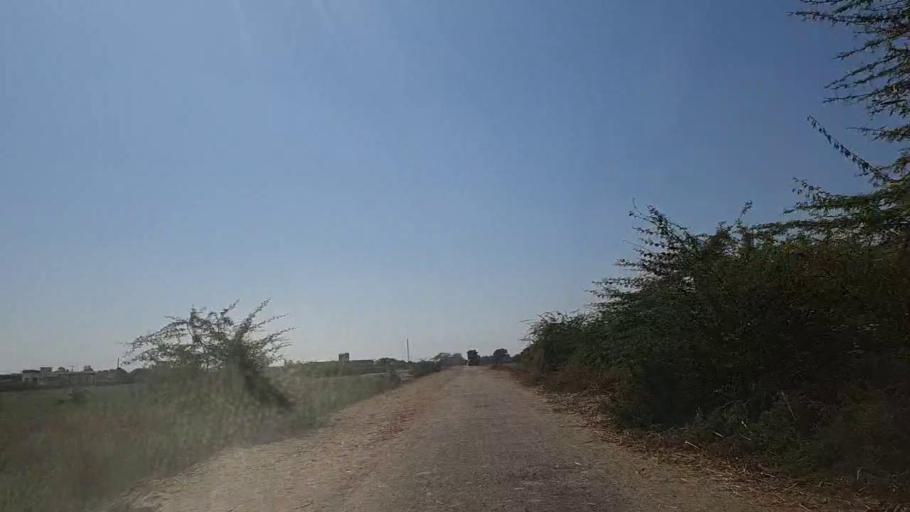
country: PK
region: Sindh
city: Naukot
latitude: 25.0604
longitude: 69.3887
